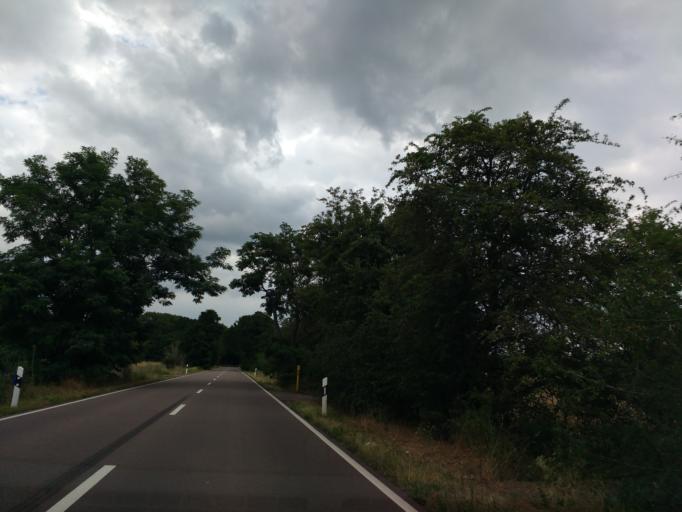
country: DE
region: Saxony-Anhalt
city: Dieskau
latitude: 51.4338
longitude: 12.0246
